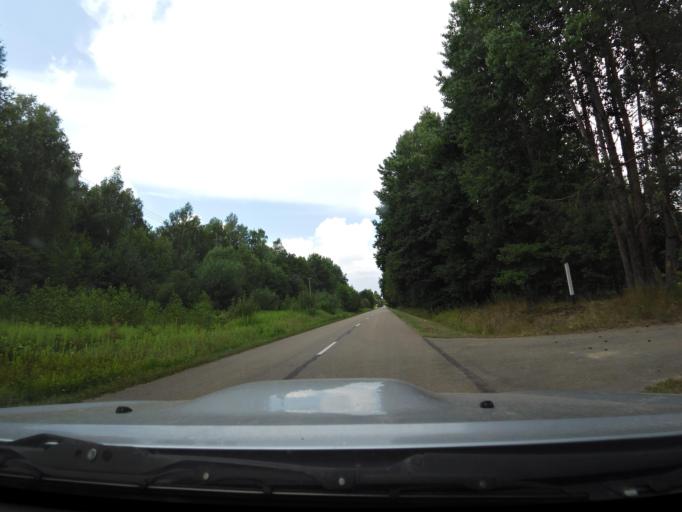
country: RU
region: Kaliningrad
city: Neman
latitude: 55.0923
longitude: 22.0275
